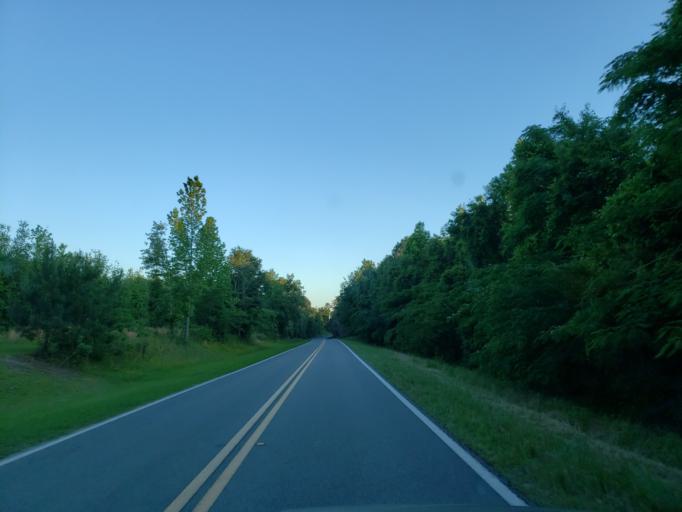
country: US
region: Florida
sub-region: Madison County
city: Madison
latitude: 30.6107
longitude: -83.2549
